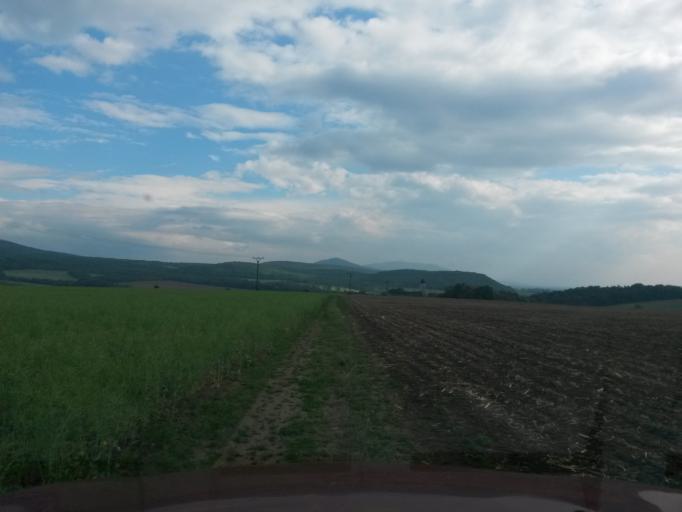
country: SK
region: Kosicky
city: Secovce
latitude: 48.7432
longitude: 21.4611
